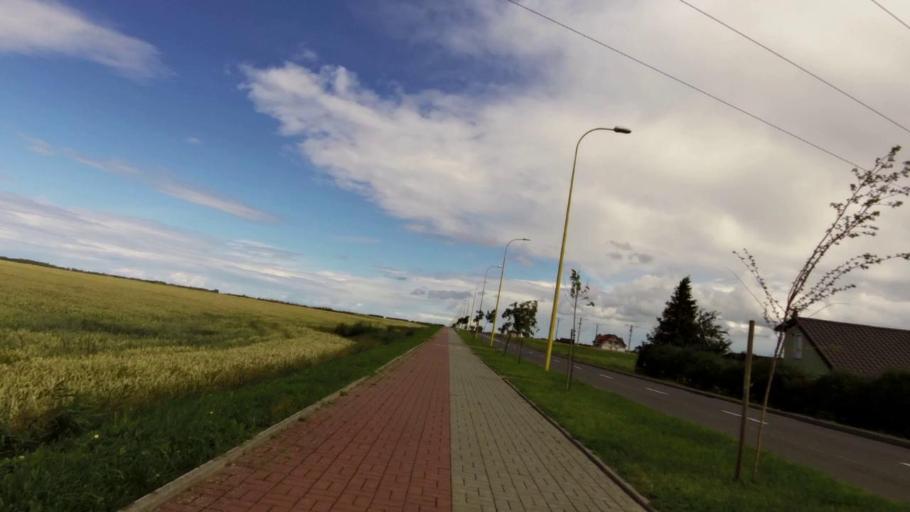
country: PL
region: West Pomeranian Voivodeship
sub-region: Powiat slawienski
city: Darlowo
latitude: 54.4325
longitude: 16.4121
